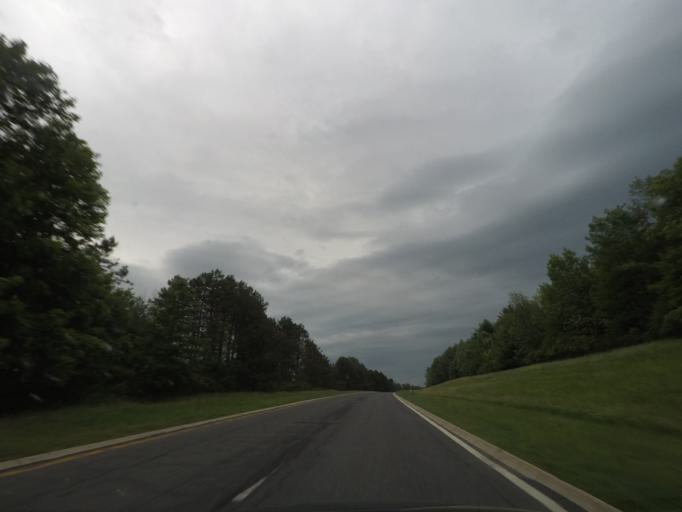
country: US
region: New York
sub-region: Columbia County
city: Philmont
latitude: 42.2725
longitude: -73.6128
